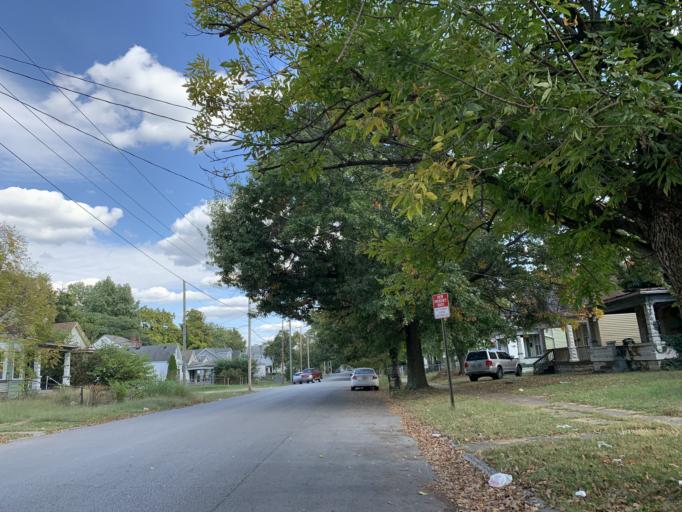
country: US
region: Kentucky
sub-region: Jefferson County
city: Louisville
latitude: 38.2445
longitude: -85.7943
